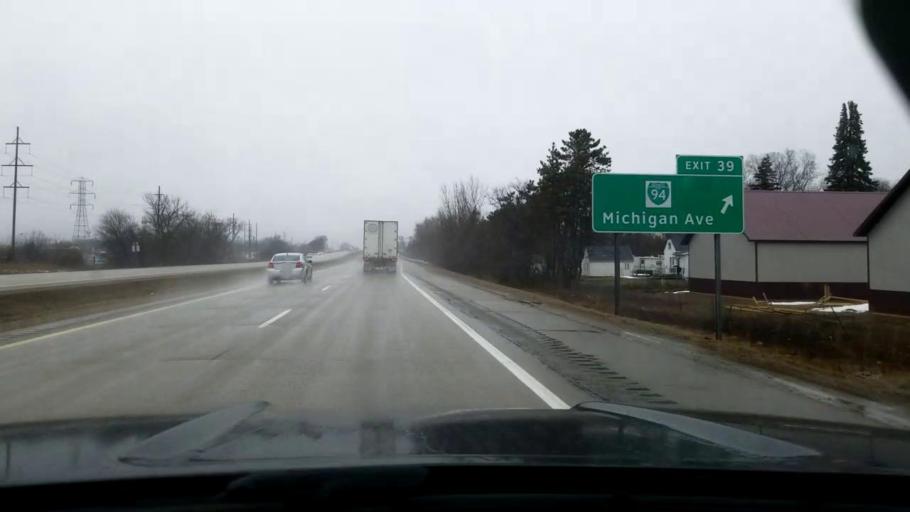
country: US
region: Michigan
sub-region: Jackson County
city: Michigan Center
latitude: 42.2522
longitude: -84.3565
